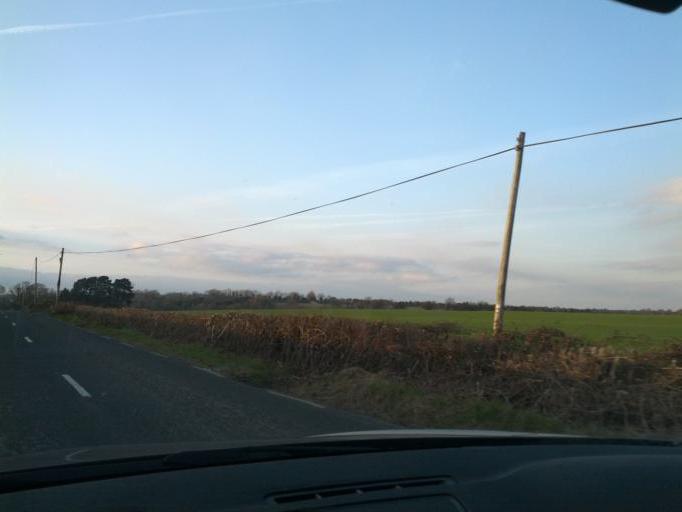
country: IE
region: Munster
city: Nenagh Bridge
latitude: 52.8888
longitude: -8.1989
